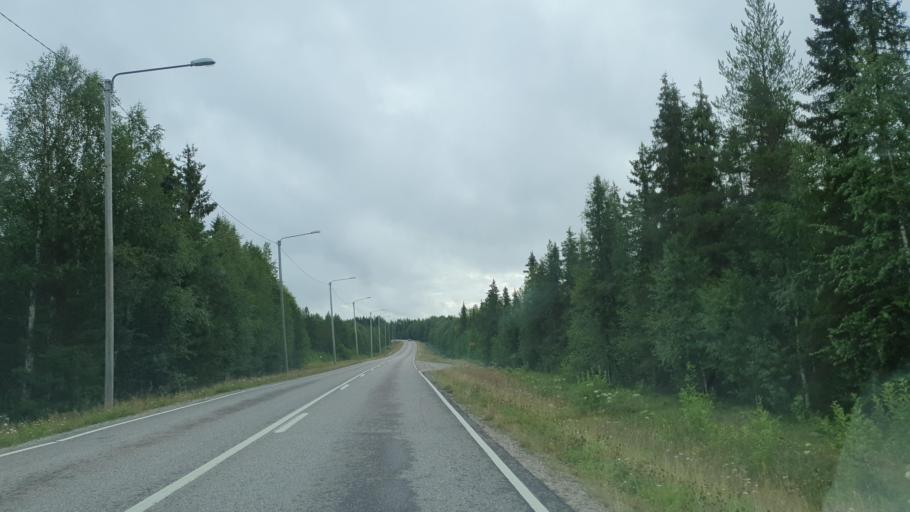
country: FI
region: Lapland
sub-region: Itae-Lappi
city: Pelkosenniemi
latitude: 66.9825
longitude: 27.5321
